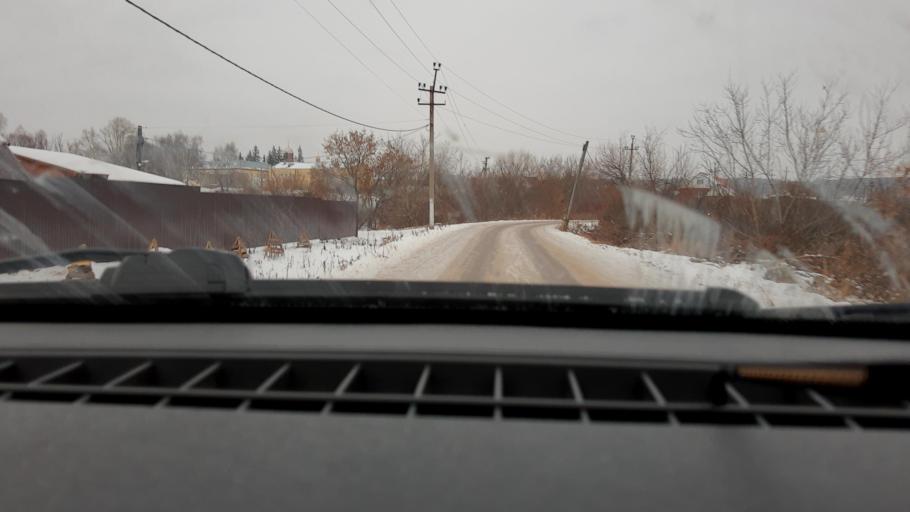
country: RU
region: Bashkortostan
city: Kabakovo
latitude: 54.7001
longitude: 56.2503
